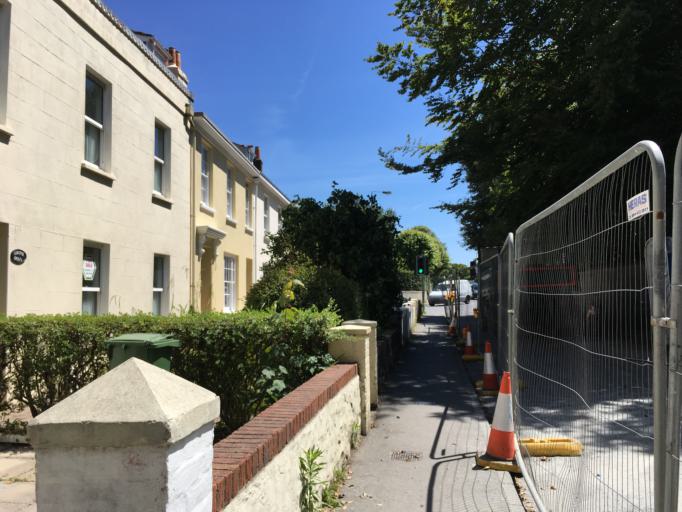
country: GG
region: St Peter Port
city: Saint Peter Port
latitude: 49.4600
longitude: -2.5446
